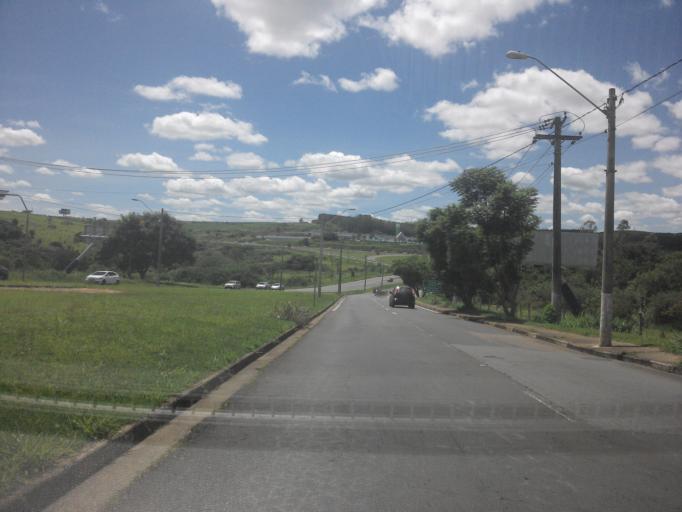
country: BR
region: Sao Paulo
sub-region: Campinas
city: Campinas
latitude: -22.8889
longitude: -47.0174
